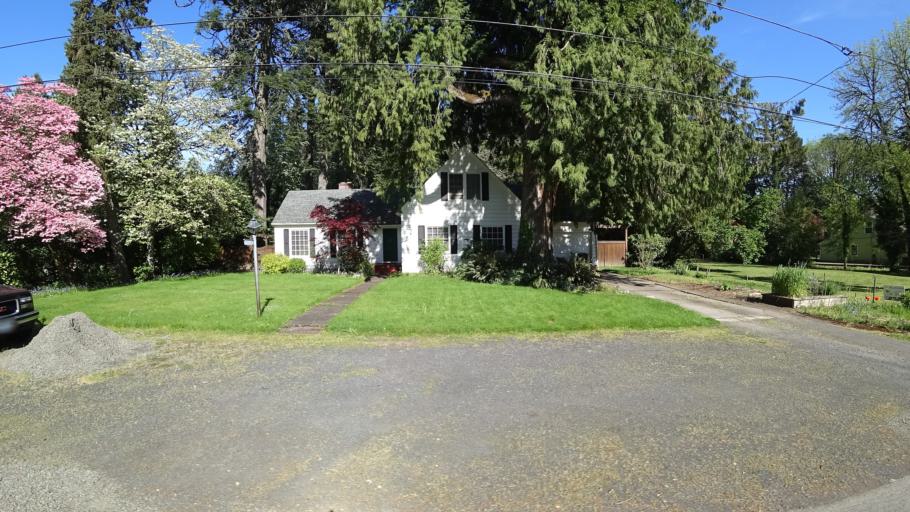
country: US
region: Oregon
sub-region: Washington County
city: Hillsboro
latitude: 45.5328
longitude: -122.9858
